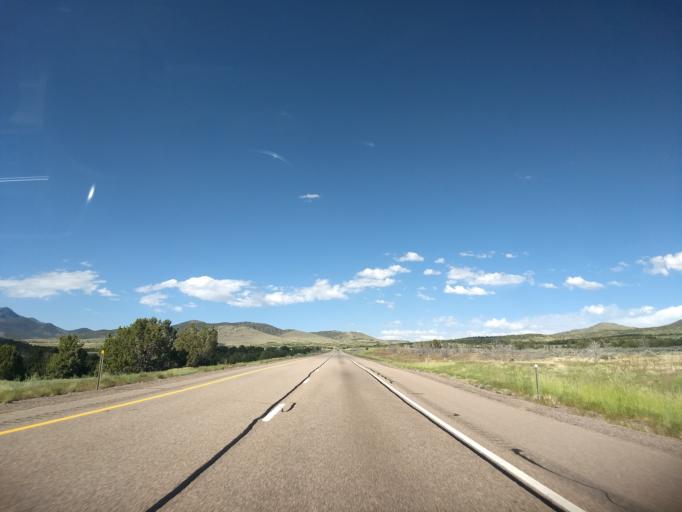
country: US
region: Utah
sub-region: Millard County
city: Fillmore
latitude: 39.1737
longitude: -112.2101
